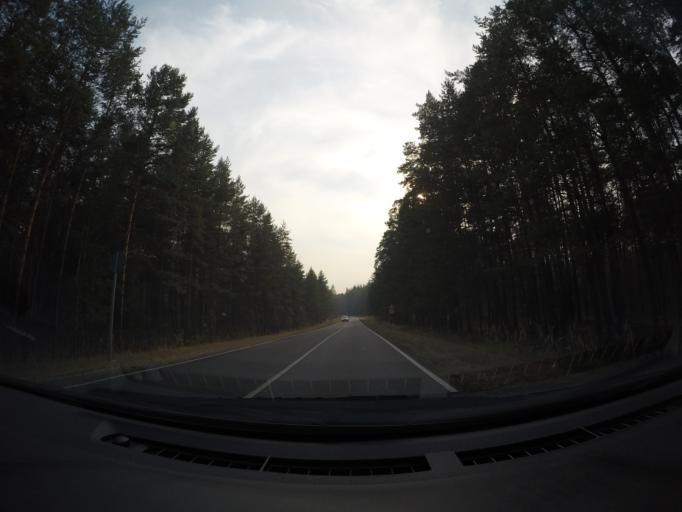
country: RU
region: Moskovskaya
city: Imeni Tsyurupy
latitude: 55.4971
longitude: 38.6905
